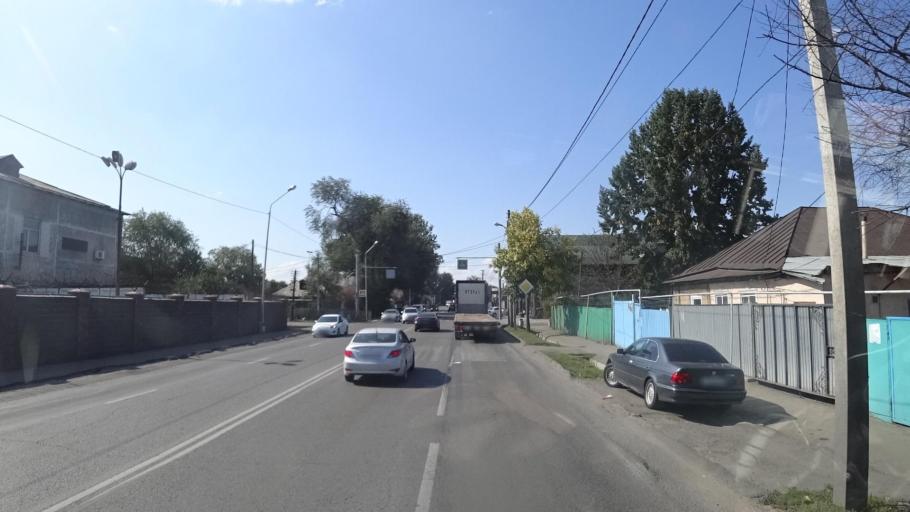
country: KZ
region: Almaty Oblysy
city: Pervomayskiy
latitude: 43.3521
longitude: 76.9573
